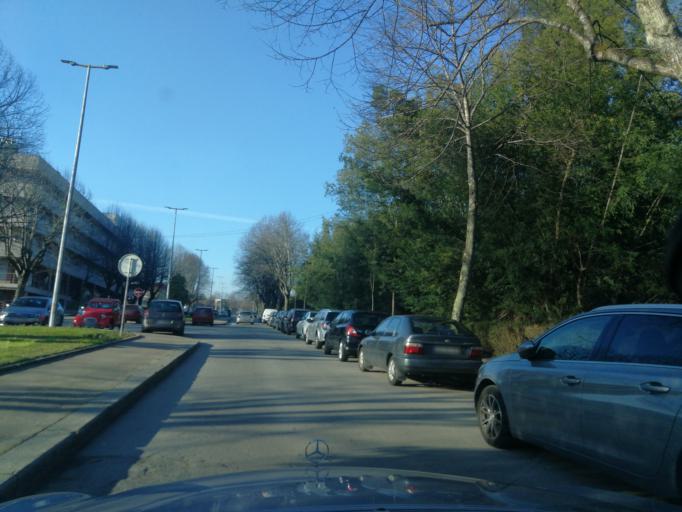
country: PT
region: Braga
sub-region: Guimaraes
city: Ponte
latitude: 41.4834
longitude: -8.3428
